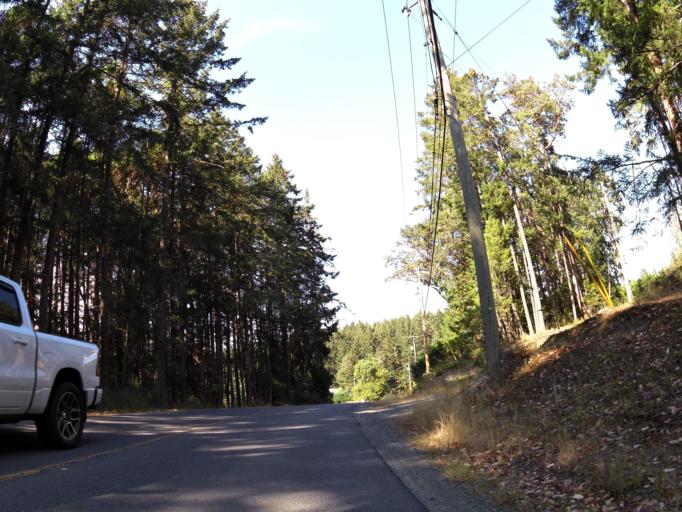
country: CA
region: British Columbia
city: North Saanich
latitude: 48.6696
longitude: -123.5535
